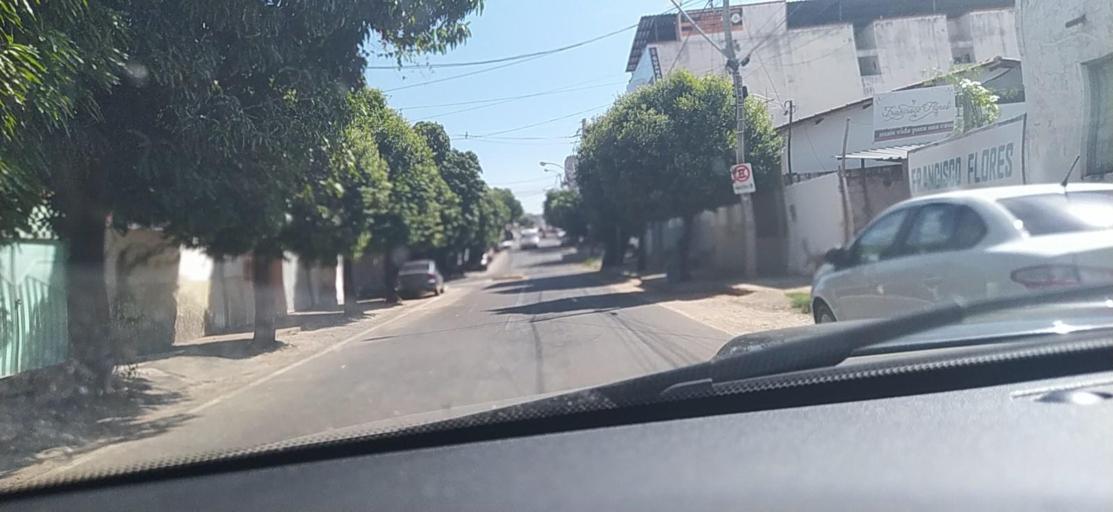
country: BR
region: Bahia
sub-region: Guanambi
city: Guanambi
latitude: -14.2201
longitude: -42.7741
